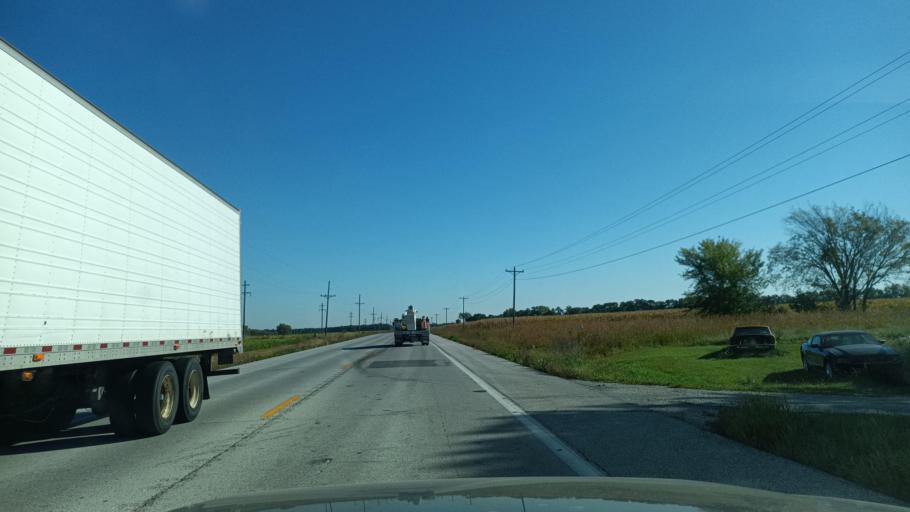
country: US
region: Missouri
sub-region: Audrain County
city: Vandalia
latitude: 39.4500
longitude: -91.6274
